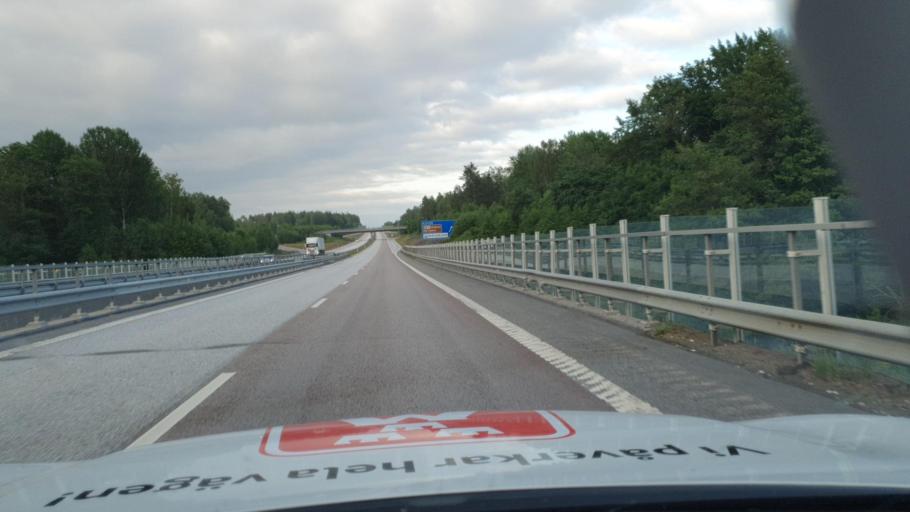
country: SE
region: Vaermland
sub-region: Karlstads Kommun
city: Skattkarr
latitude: 59.4007
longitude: 13.6059
